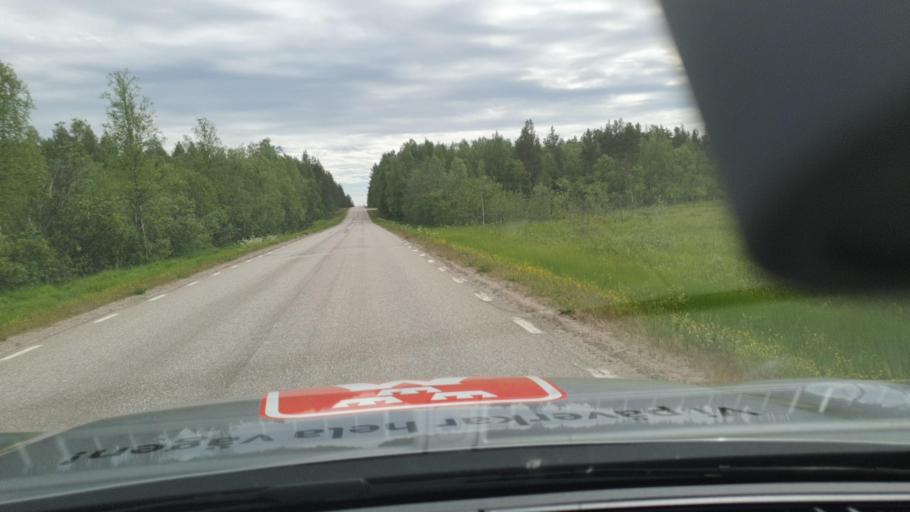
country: SE
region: Norrbotten
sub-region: Kalix Kommun
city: Kalix
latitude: 65.9151
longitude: 23.1732
